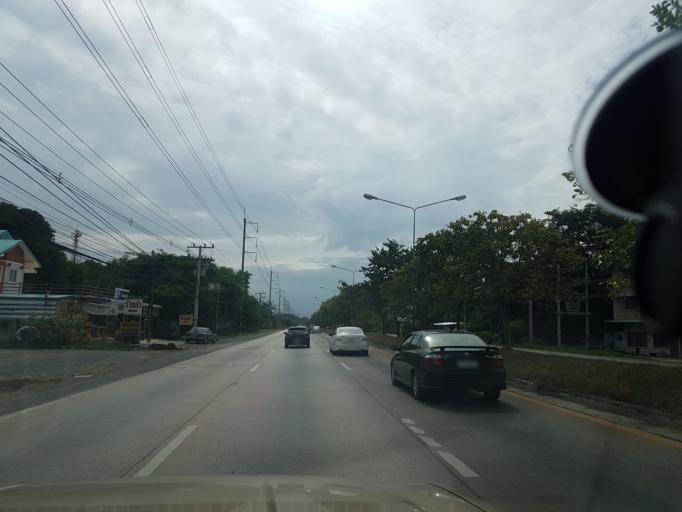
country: TH
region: Sara Buri
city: Phra Phutthabat
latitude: 14.7140
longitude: 100.8219
